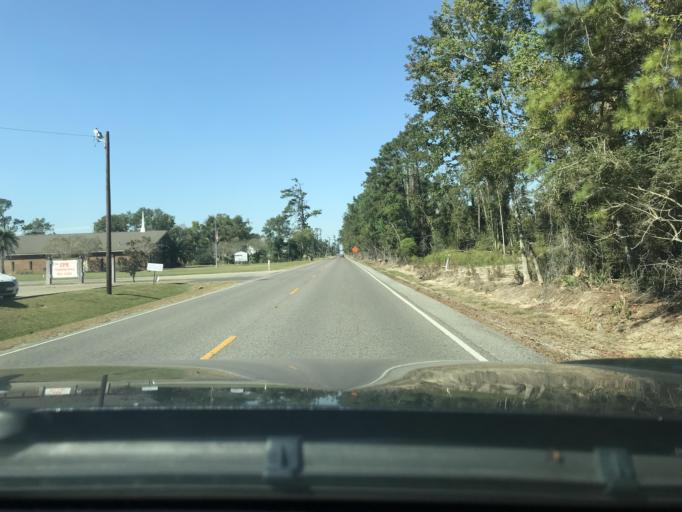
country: US
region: Louisiana
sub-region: Calcasieu Parish
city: Moss Bluff
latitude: 30.3037
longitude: -93.2001
